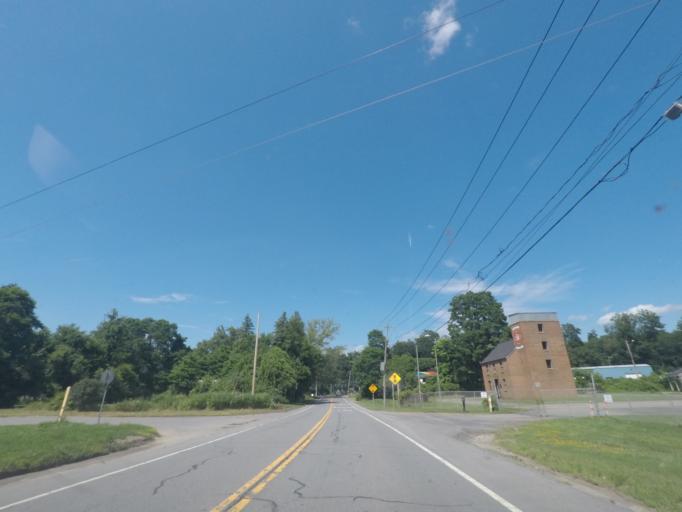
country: US
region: New York
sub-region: Schenectady County
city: Rotterdam
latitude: 42.8036
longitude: -73.9914
